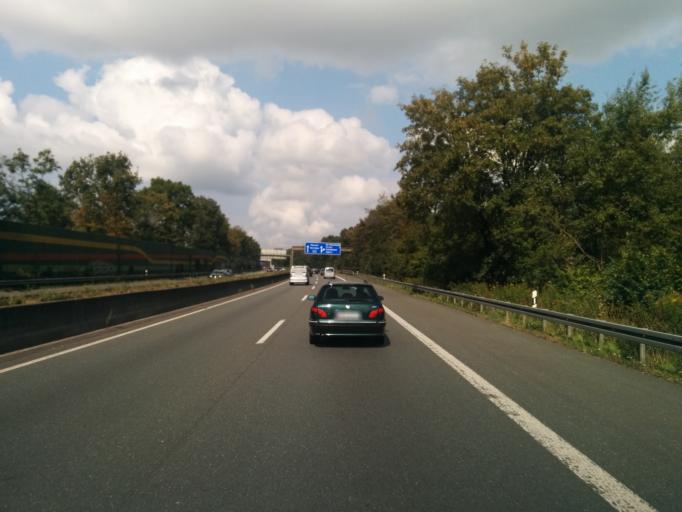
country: DE
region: North Rhine-Westphalia
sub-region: Regierungsbezirk Munster
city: Recklinghausen
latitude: 51.5951
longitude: 7.1866
